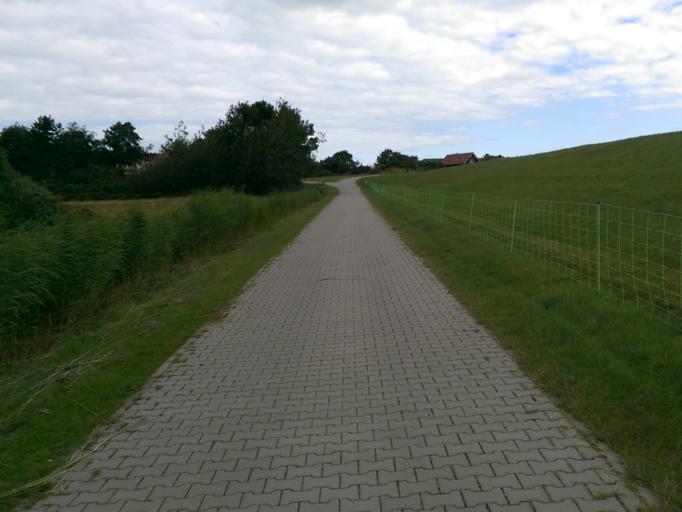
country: DE
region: Lower Saxony
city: Spiekeroog
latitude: 53.7686
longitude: 7.7041
